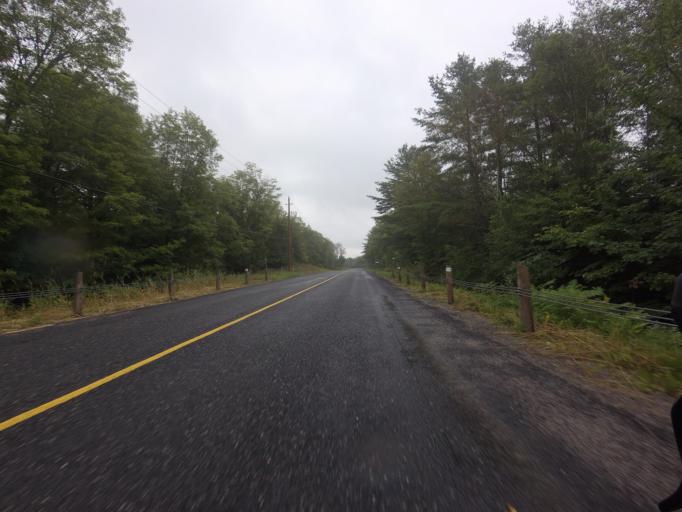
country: CA
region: Ontario
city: Perth
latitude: 45.0675
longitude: -76.5034
